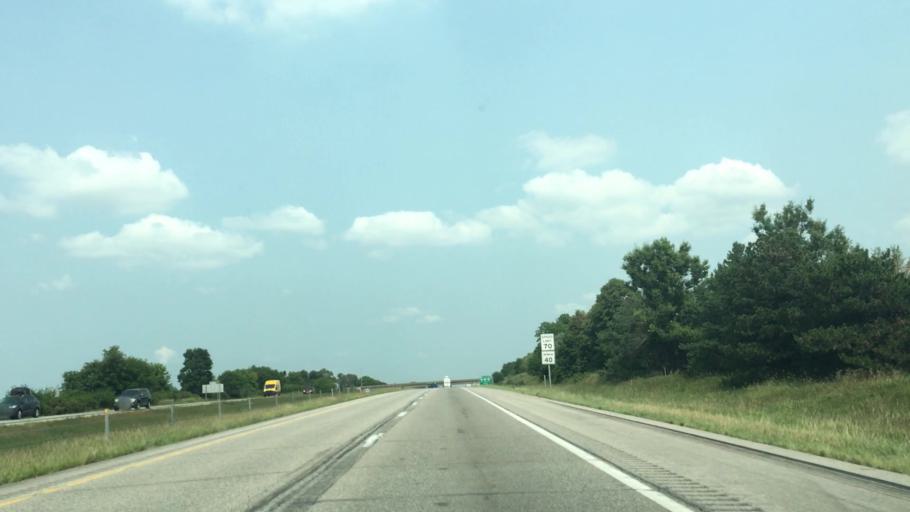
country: US
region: Iowa
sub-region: Linn County
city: Ely
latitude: 41.9007
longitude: -91.6715
